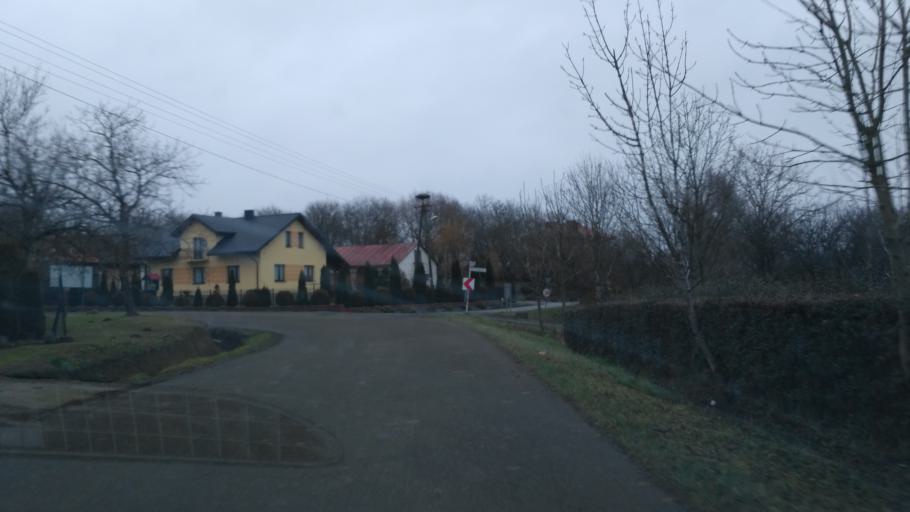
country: PL
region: Subcarpathian Voivodeship
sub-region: Powiat jaroslawski
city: Pruchnik
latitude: 49.9145
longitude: 22.5341
